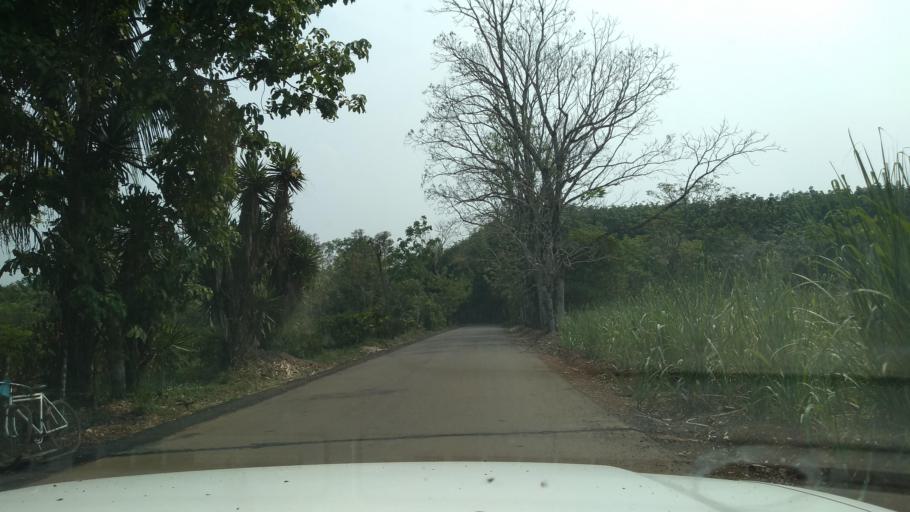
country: MX
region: Veracruz
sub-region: Tezonapa
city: Laguna Chica (Pueblo Nuevo)
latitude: 18.5360
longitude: -96.7857
